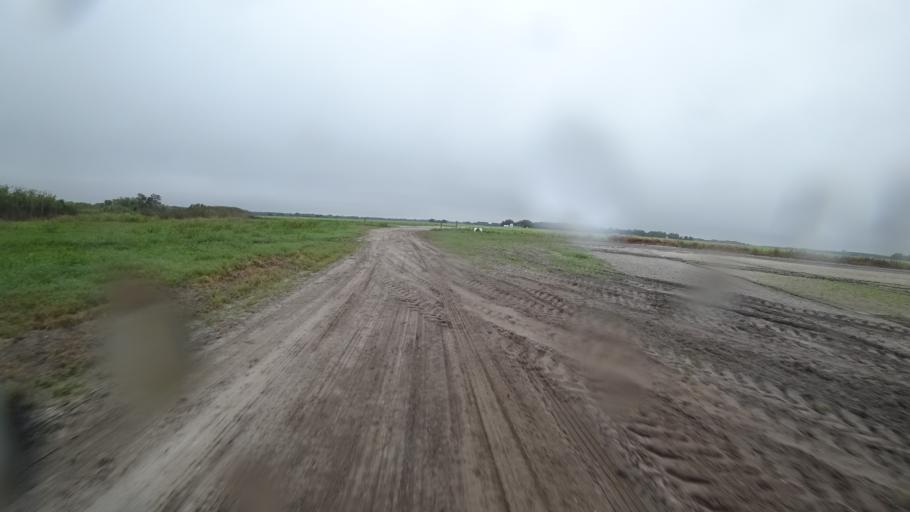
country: US
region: Florida
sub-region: Sarasota County
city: Warm Mineral Springs
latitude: 27.2960
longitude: -82.1611
